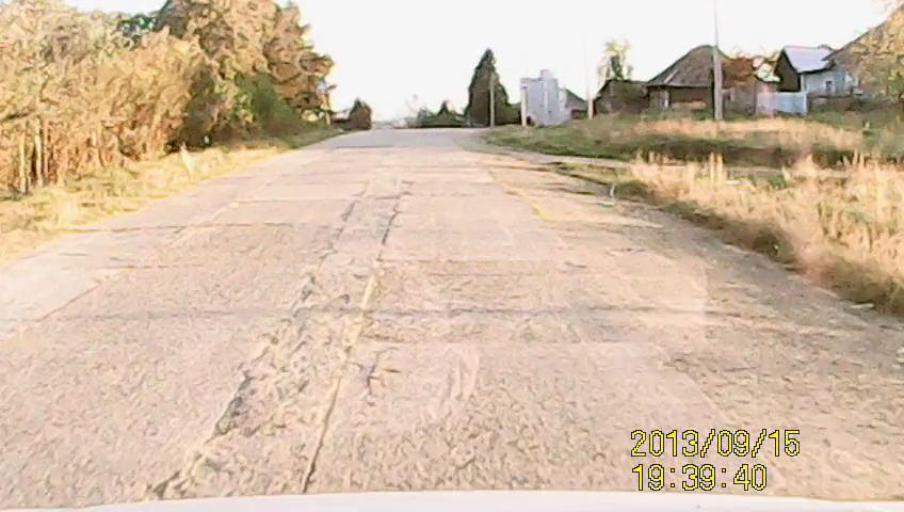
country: RU
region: Chelyabinsk
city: Kyshtym
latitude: 55.8509
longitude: 60.4815
